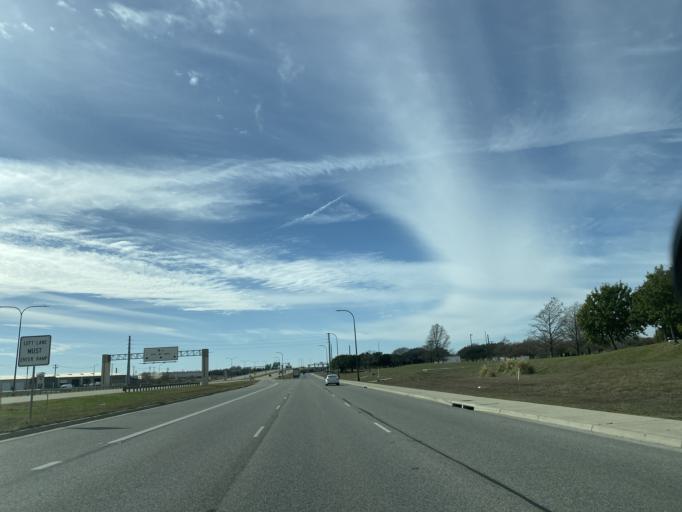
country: US
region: Texas
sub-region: Travis County
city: Manor
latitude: 30.3331
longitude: -97.6148
